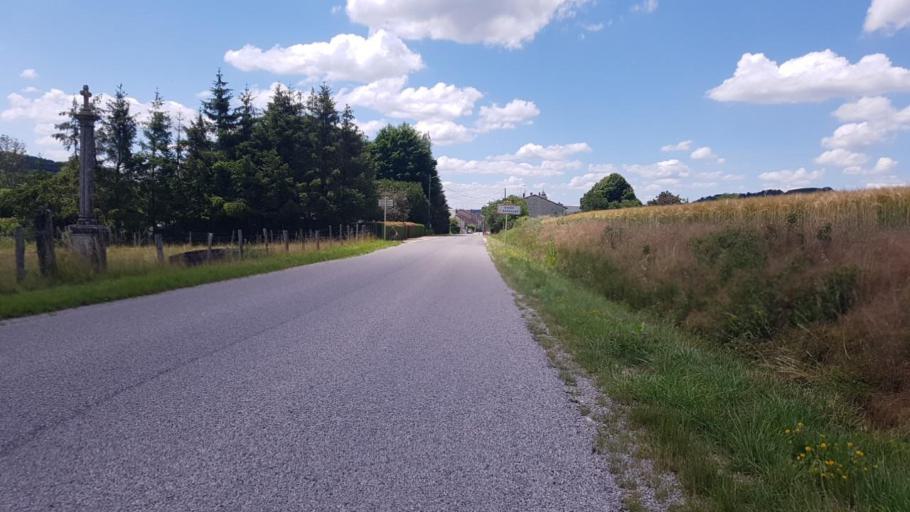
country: FR
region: Lorraine
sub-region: Departement de la Meuse
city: Vacon
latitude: 48.6472
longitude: 5.5172
